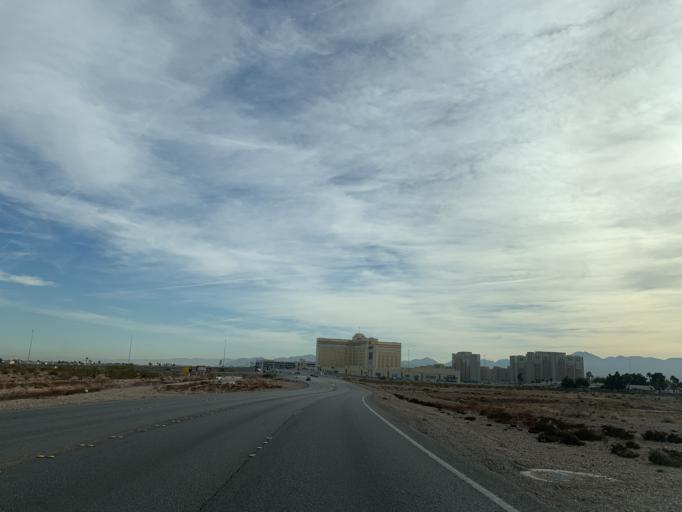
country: US
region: Nevada
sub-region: Clark County
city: Enterprise
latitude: 36.0134
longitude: -115.1878
